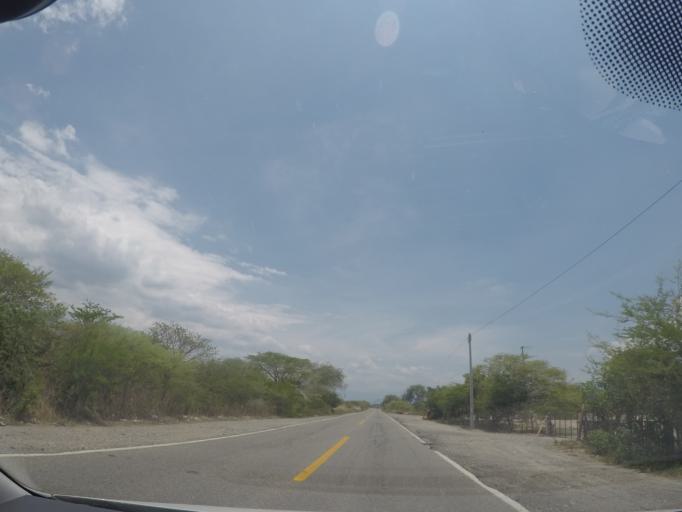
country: MX
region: Oaxaca
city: Magdalena Tequisistlan
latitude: 16.4104
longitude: -95.5715
